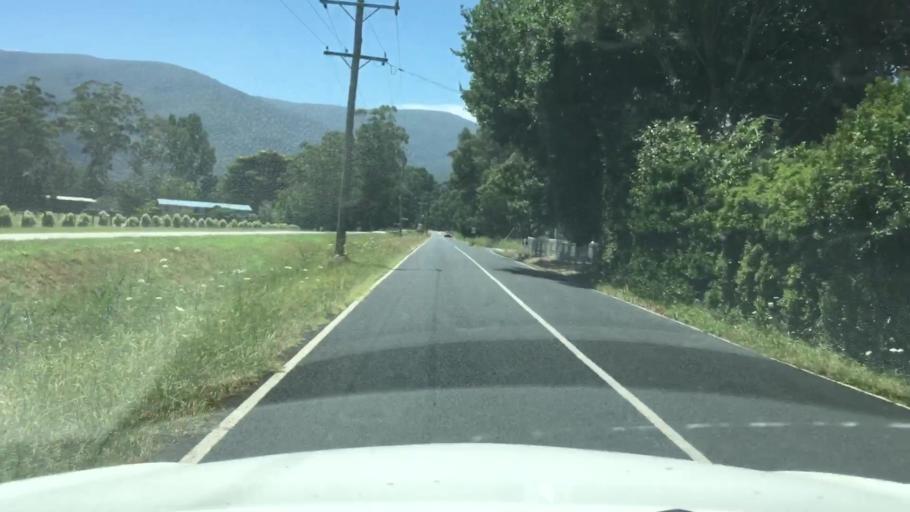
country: AU
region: Victoria
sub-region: Yarra Ranges
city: Millgrove
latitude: -37.7676
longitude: 145.6356
